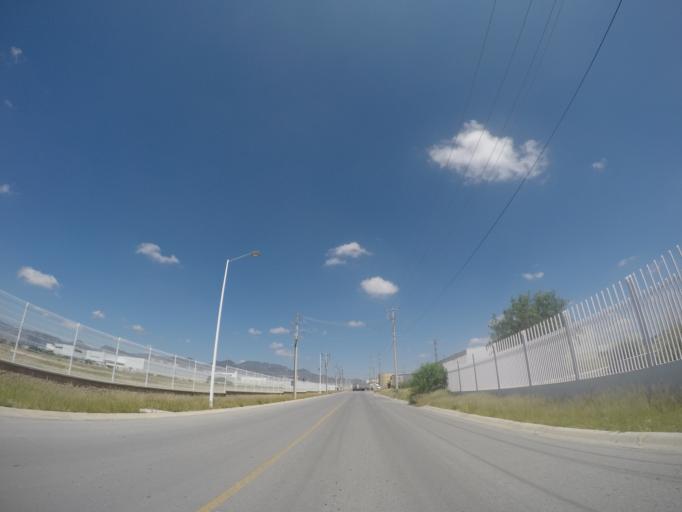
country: MX
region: San Luis Potosi
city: La Pila
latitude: 21.9716
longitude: -100.8755
